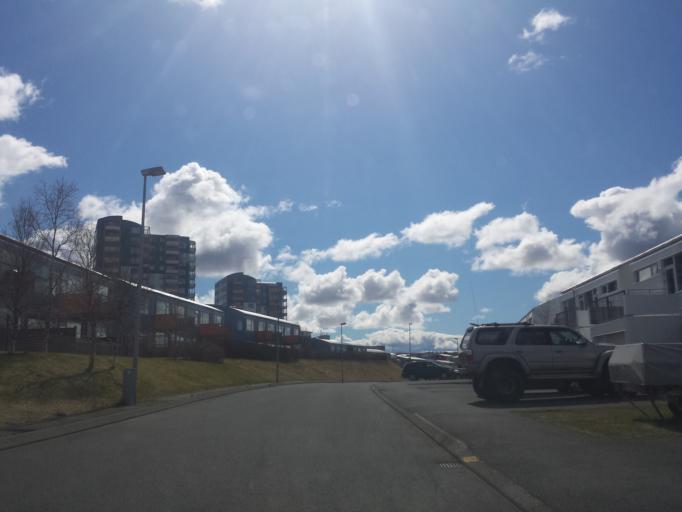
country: IS
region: Capital Region
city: Reykjavik
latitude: 64.0963
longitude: -21.8573
